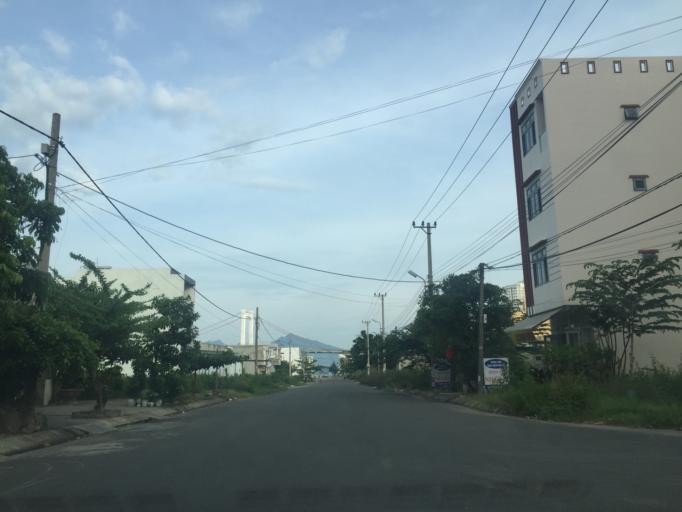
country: VN
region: Da Nang
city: Da Nang
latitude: 16.0922
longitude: 108.2278
